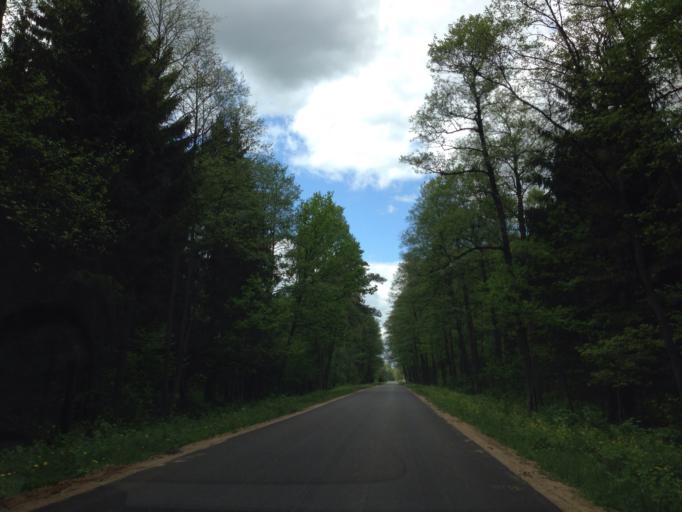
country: PL
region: Podlasie
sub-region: Powiat moniecki
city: Goniadz
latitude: 53.3663
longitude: 22.5946
